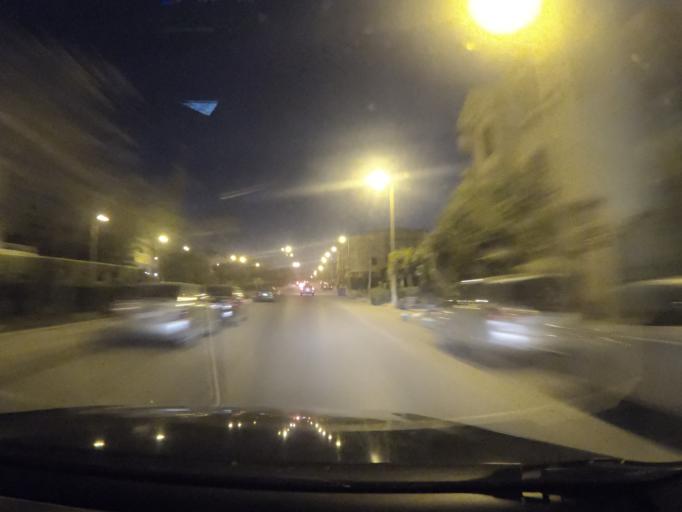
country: EG
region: Muhafazat al Qahirah
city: Cairo
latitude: 30.0139
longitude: 31.4239
